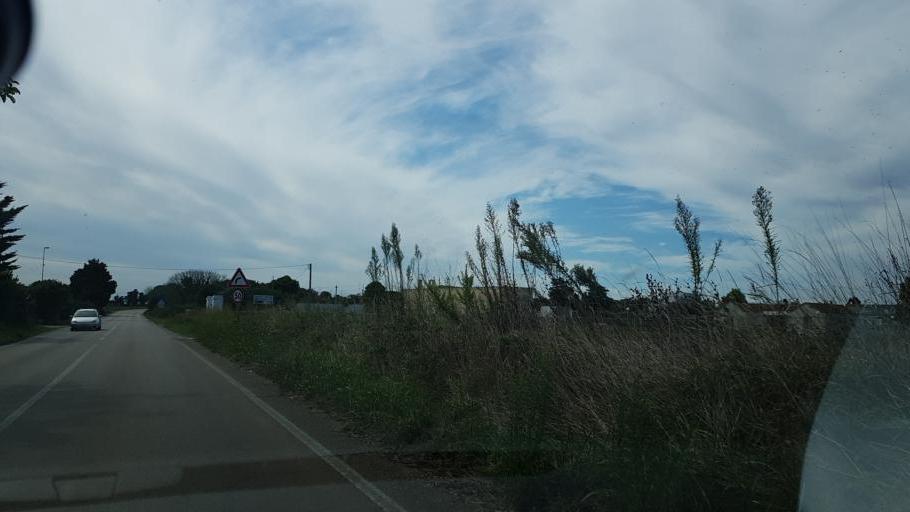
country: IT
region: Apulia
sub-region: Provincia di Lecce
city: Borgagne
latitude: 40.2312
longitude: 18.4435
